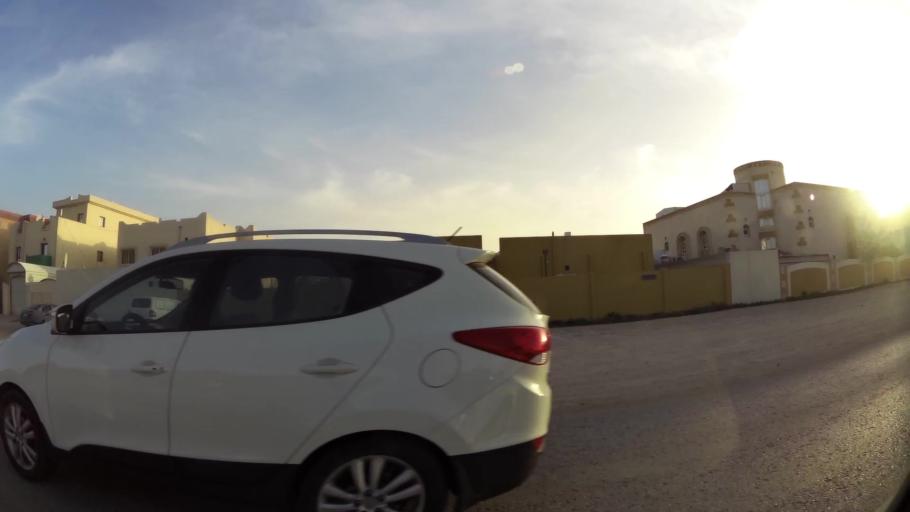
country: QA
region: Al Wakrah
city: Al Wakrah
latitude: 25.1496
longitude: 51.6051
